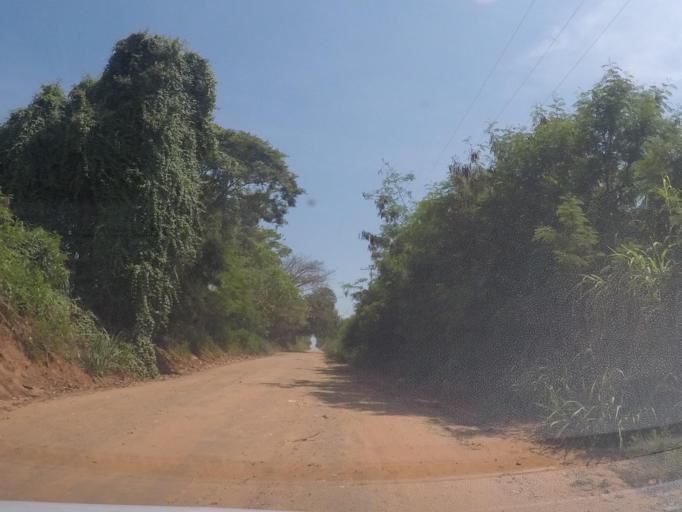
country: BR
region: Sao Paulo
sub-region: Sumare
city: Sumare
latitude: -22.8507
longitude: -47.2726
